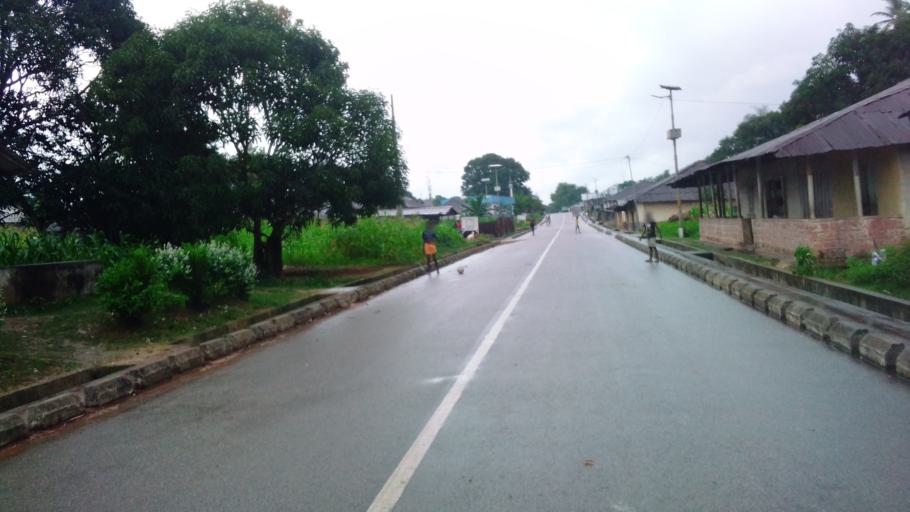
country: SL
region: Northern Province
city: Lunsar
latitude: 8.6807
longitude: -12.5306
